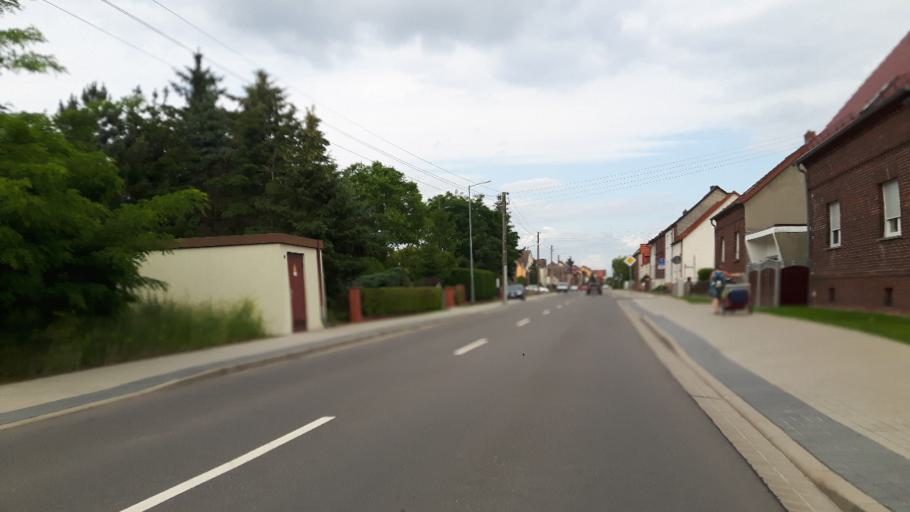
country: DE
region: Saxony-Anhalt
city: Wittenburg
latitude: 51.8458
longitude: 12.6202
